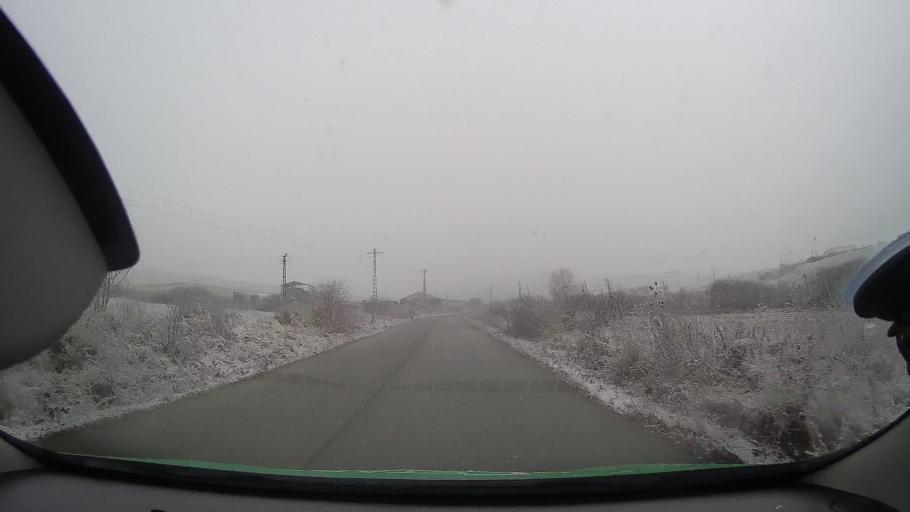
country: RO
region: Alba
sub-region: Comuna Noslac
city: Noslac
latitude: 46.3771
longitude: 23.9054
